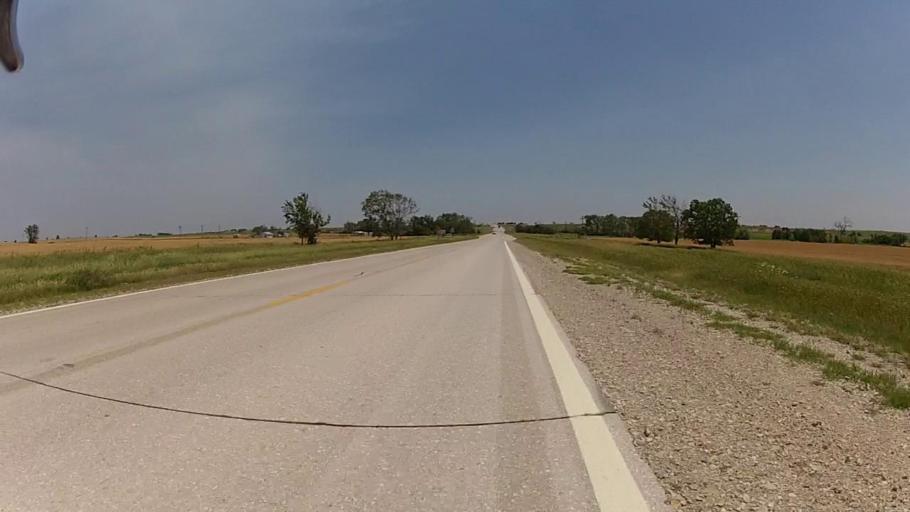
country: US
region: Kansas
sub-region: Sumner County
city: Wellington
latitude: 37.0576
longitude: -97.3494
